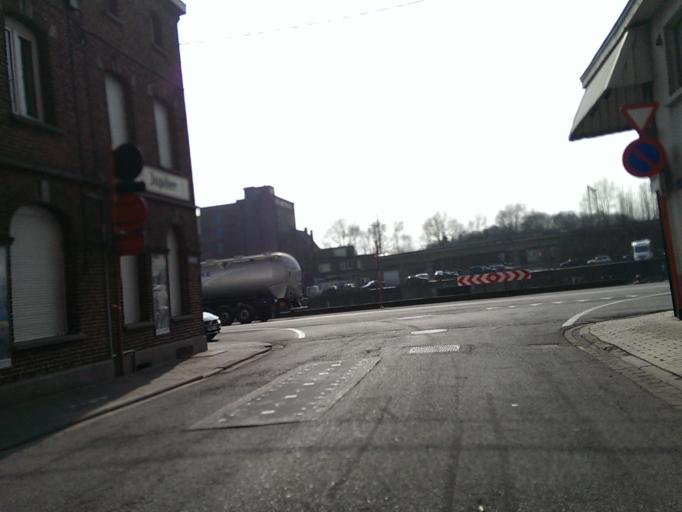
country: BE
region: Flanders
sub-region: Provincie West-Vlaanderen
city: Roeselare
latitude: 50.9451
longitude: 3.1344
